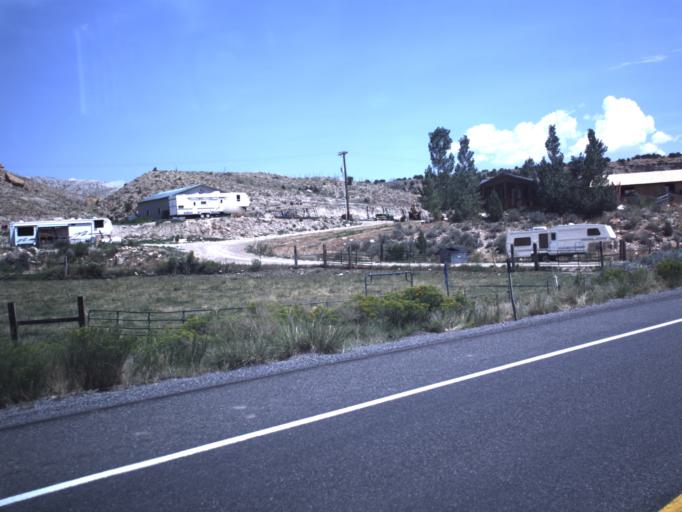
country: US
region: Utah
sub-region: Emery County
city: Huntington
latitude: 39.3609
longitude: -111.0331
